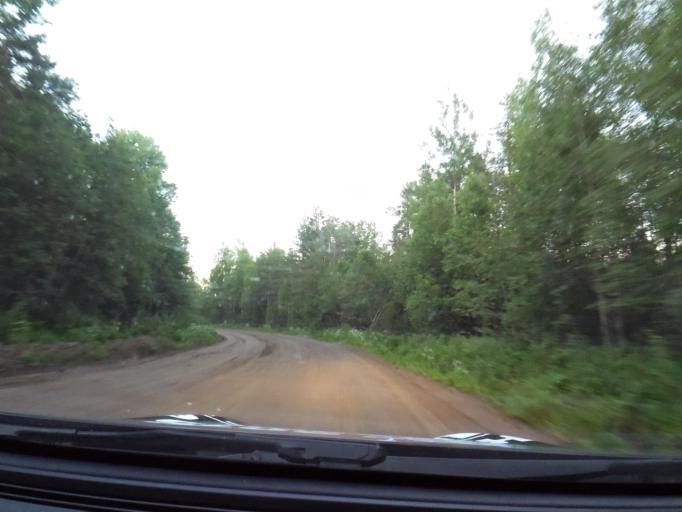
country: RU
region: Leningrad
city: Voznesen'ye
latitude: 60.8557
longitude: 35.9246
